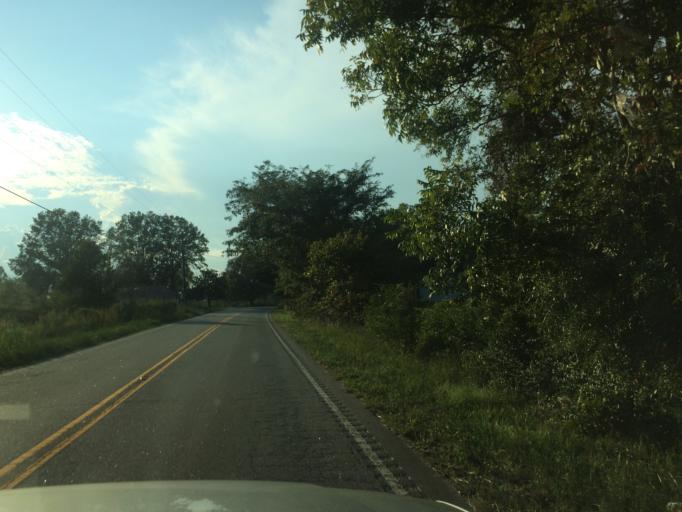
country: US
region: South Carolina
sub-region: Anderson County
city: Williamston
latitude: 34.6590
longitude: -82.5019
